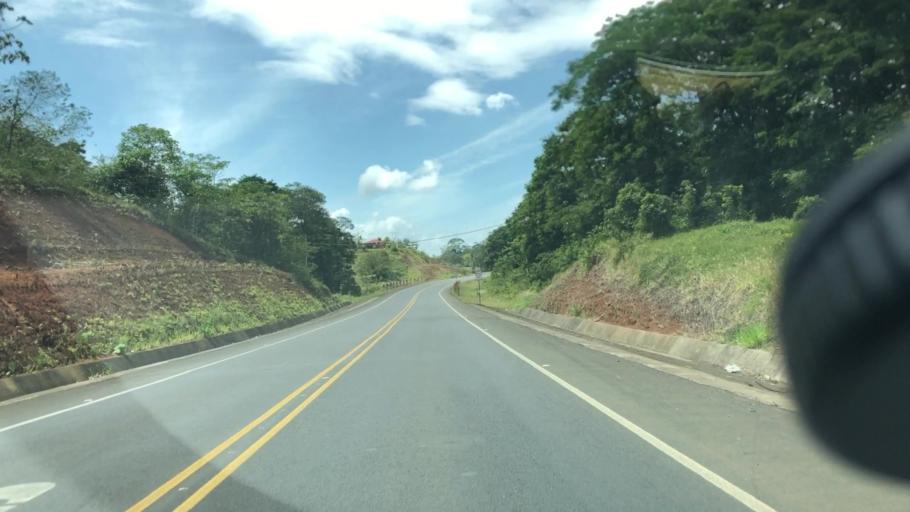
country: CR
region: Heredia
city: La Virgen
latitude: 10.4394
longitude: -84.1638
